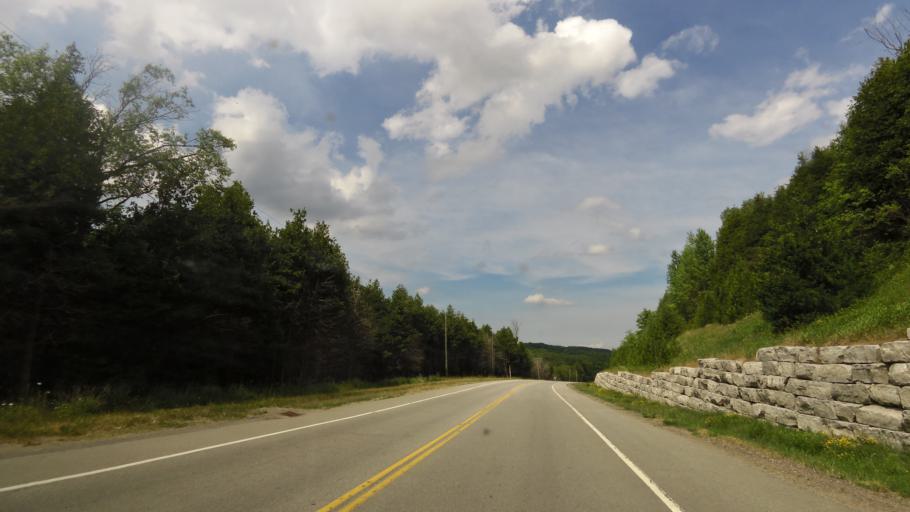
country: CA
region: Ontario
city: Orangeville
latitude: 43.9516
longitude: -80.0878
